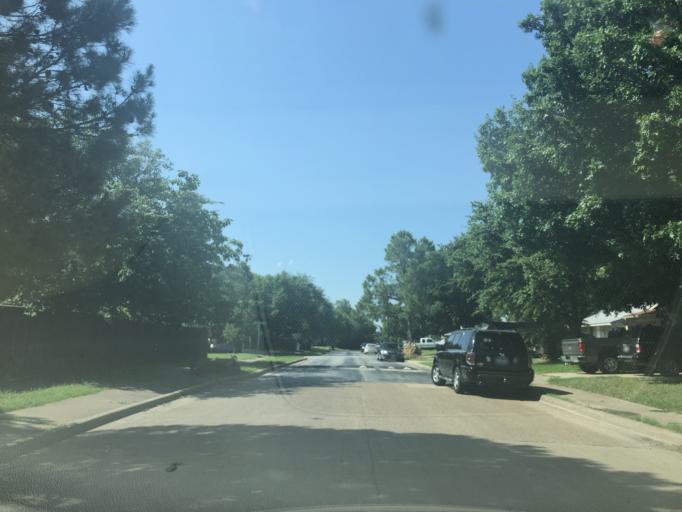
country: US
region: Texas
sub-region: Dallas County
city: Grand Prairie
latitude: 32.7179
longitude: -97.0016
